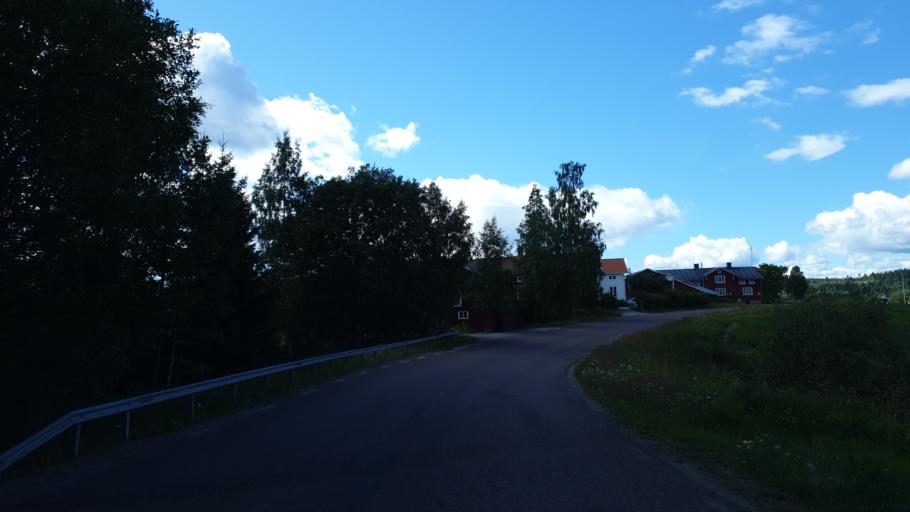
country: SE
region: Gaevleborg
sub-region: Nordanstigs Kommun
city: Bergsjoe
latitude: 62.0473
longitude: 17.2396
